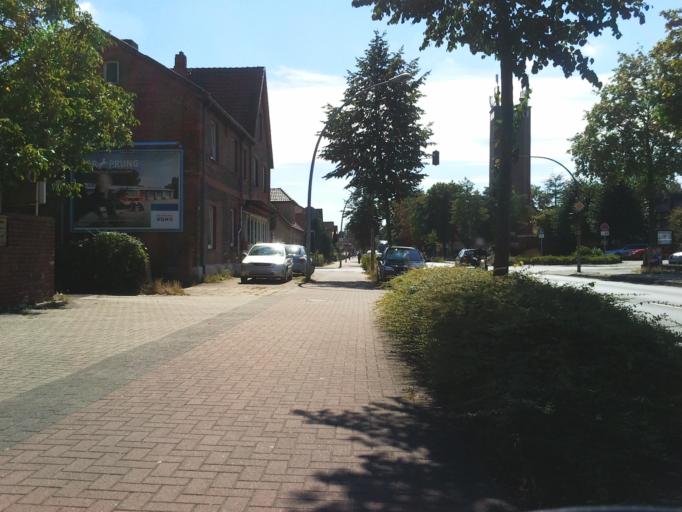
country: DE
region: Lower Saxony
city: Nienburg
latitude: 52.6600
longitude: 9.2208
